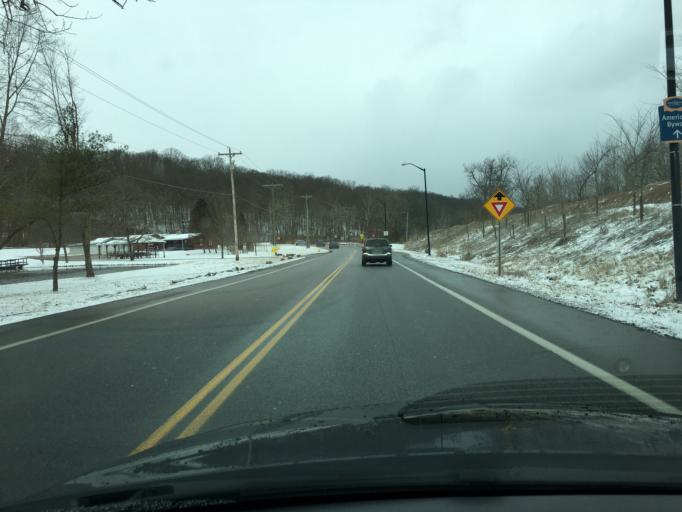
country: US
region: Ohio
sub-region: Summit County
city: Fairlawn
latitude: 41.1397
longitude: -81.5628
